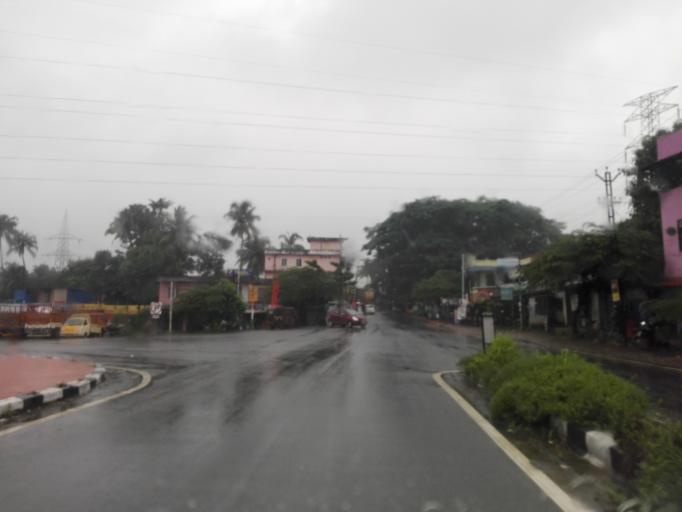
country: IN
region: Kerala
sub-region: Ernakulam
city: Elur
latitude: 10.0678
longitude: 76.3226
